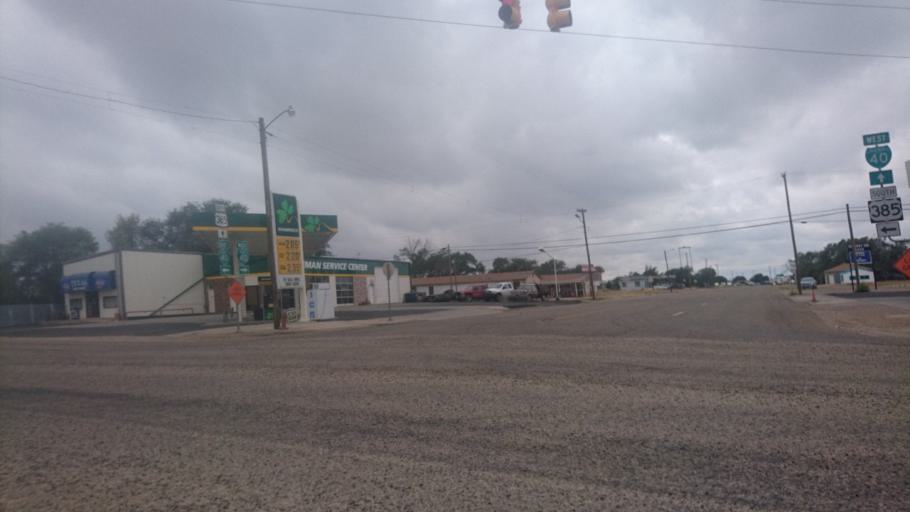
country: US
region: Texas
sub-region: Oldham County
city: Vega
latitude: 35.2431
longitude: -102.4283
